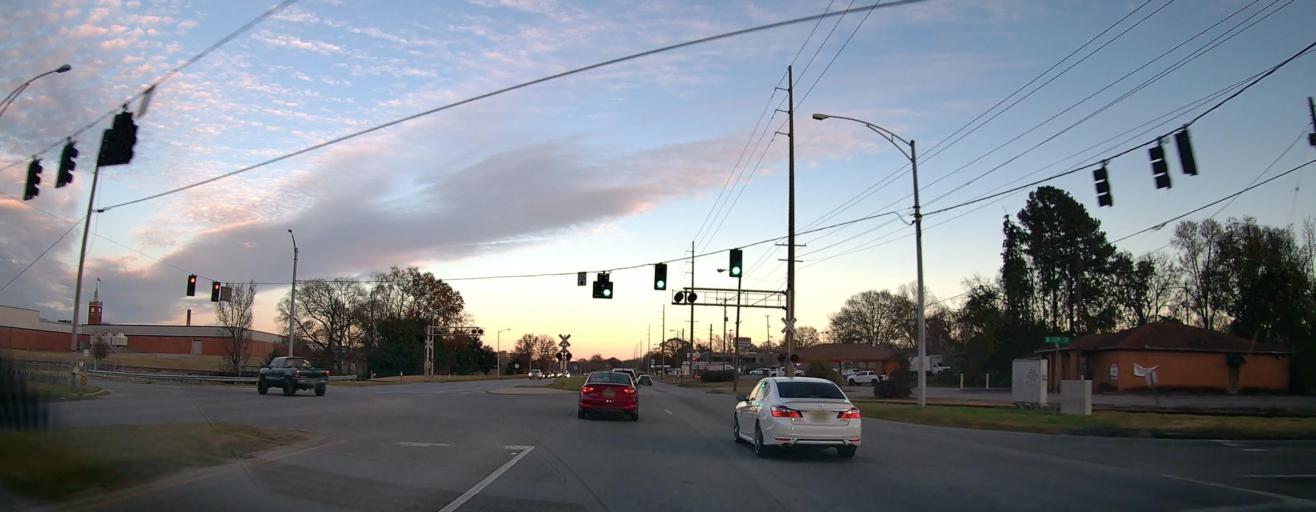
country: US
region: Alabama
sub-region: Etowah County
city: Gadsden
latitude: 34.0081
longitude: -85.9830
